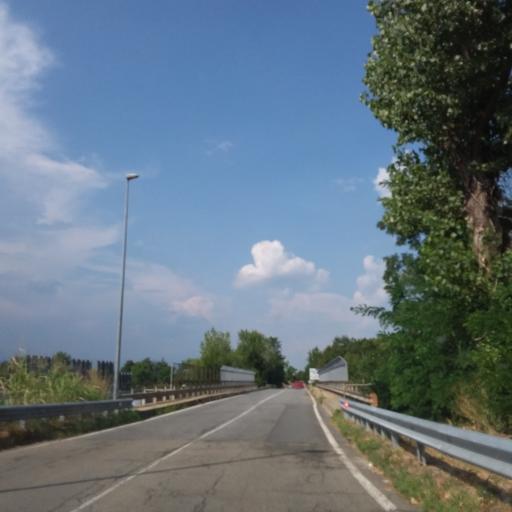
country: IT
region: Piedmont
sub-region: Provincia di Torino
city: Rivoli
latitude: 45.0812
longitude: 7.5425
